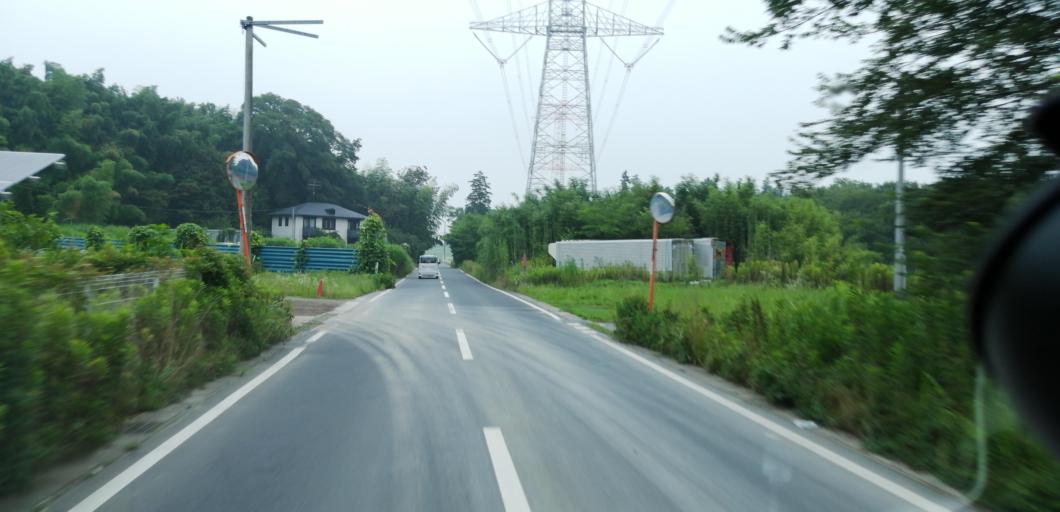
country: JP
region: Chiba
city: Noda
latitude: 35.9683
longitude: 139.9040
